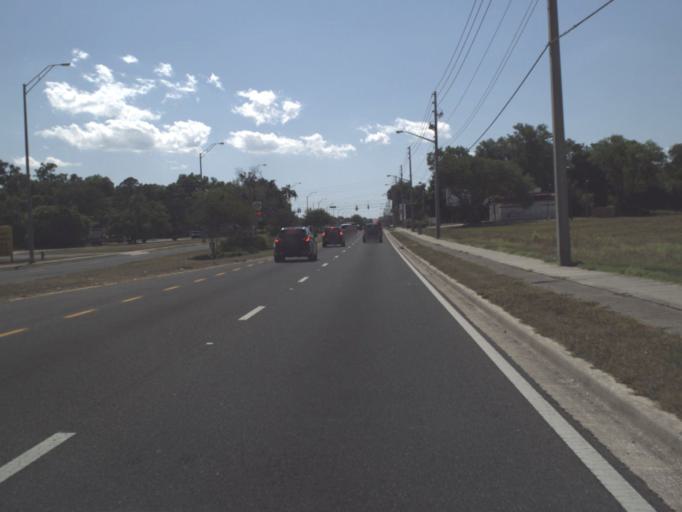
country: US
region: Florida
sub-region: Marion County
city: Ocala
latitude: 29.1864
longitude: -82.1741
